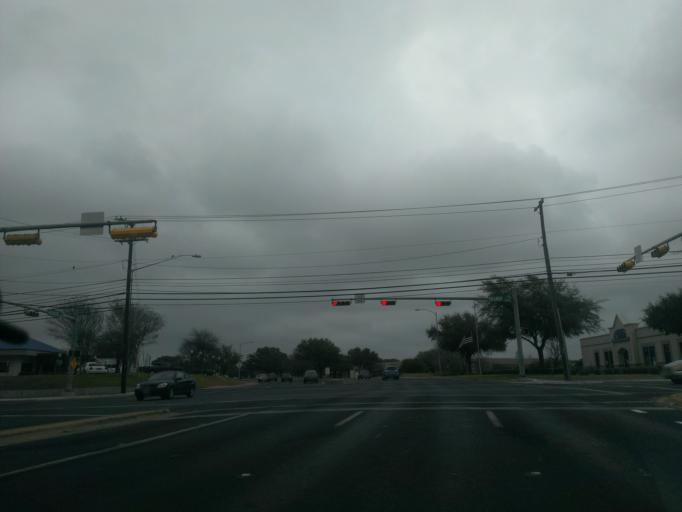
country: US
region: Texas
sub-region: Travis County
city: Wells Branch
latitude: 30.3907
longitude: -97.7144
